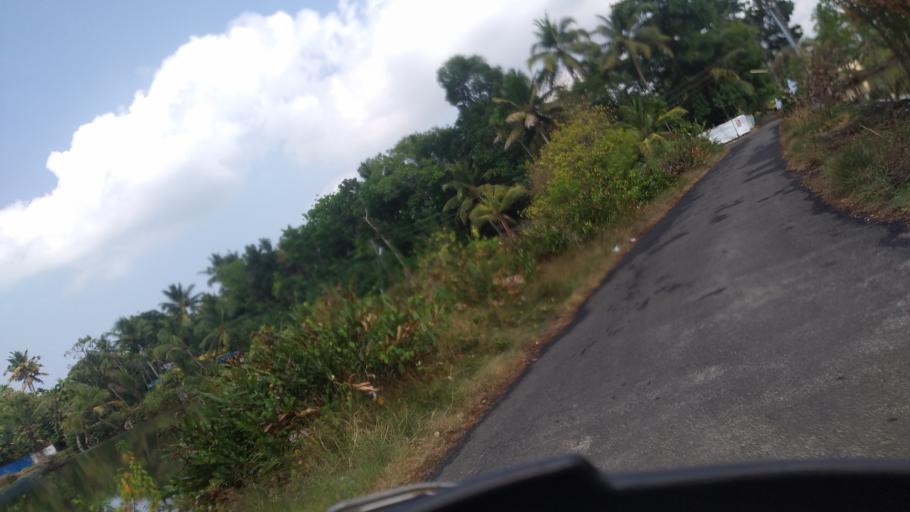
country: IN
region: Kerala
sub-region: Thrissur District
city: Kodungallur
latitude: 10.1355
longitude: 76.2112
